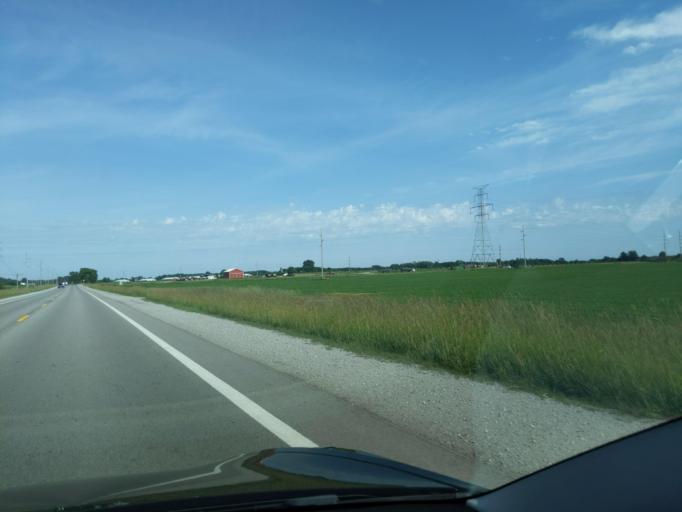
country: US
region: Michigan
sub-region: Newaygo County
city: Fremont
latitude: 43.4241
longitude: -86.0526
